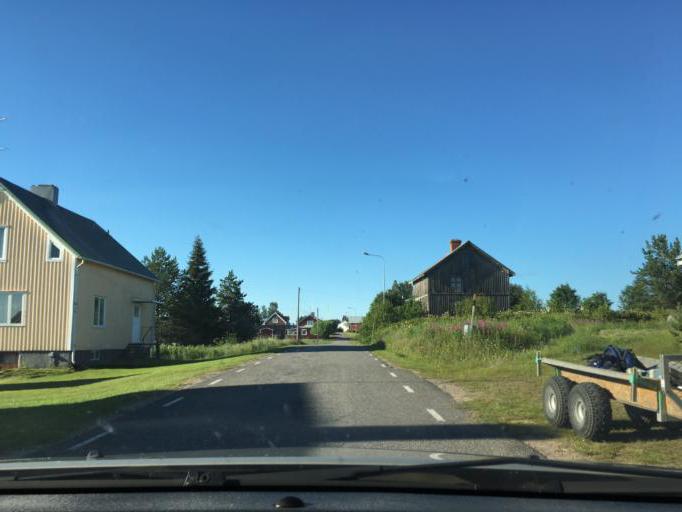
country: SE
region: Norrbotten
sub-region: Kalix Kommun
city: Toere
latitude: 66.1040
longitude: 22.7815
